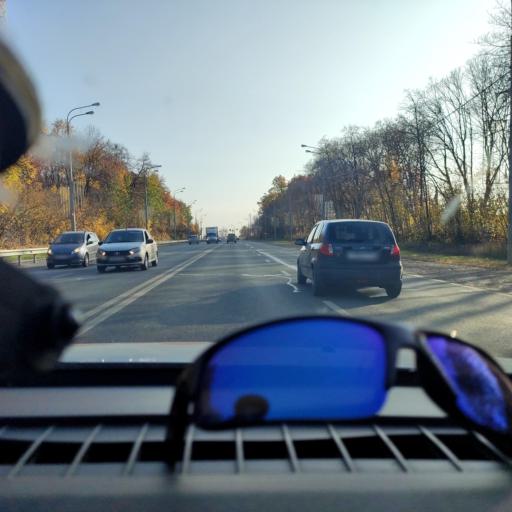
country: RU
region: Samara
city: Samara
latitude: 53.2948
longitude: 50.2250
